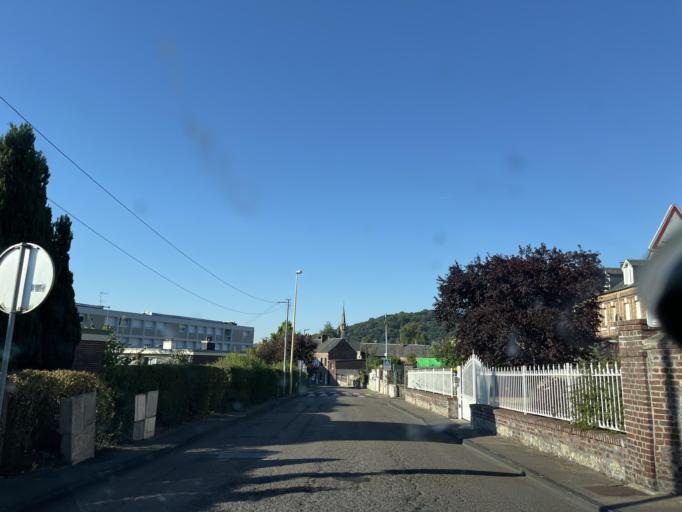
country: FR
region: Haute-Normandie
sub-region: Departement de la Seine-Maritime
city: Lillebonne
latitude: 49.5226
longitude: 0.5367
